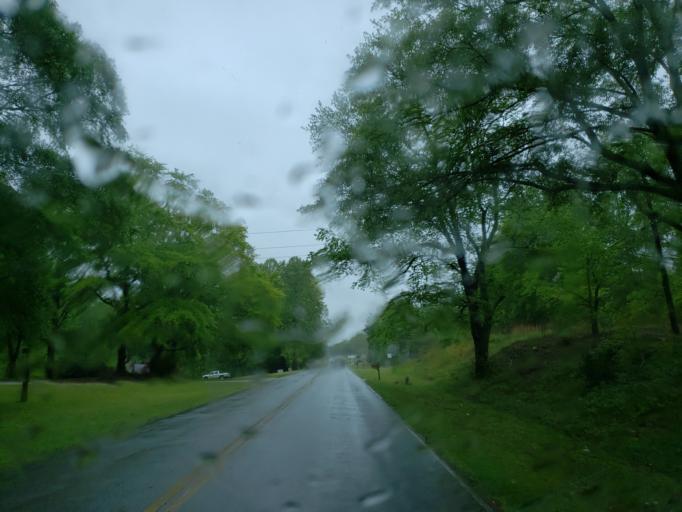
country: US
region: Georgia
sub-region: Haralson County
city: Bremen
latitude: 33.6955
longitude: -85.1873
